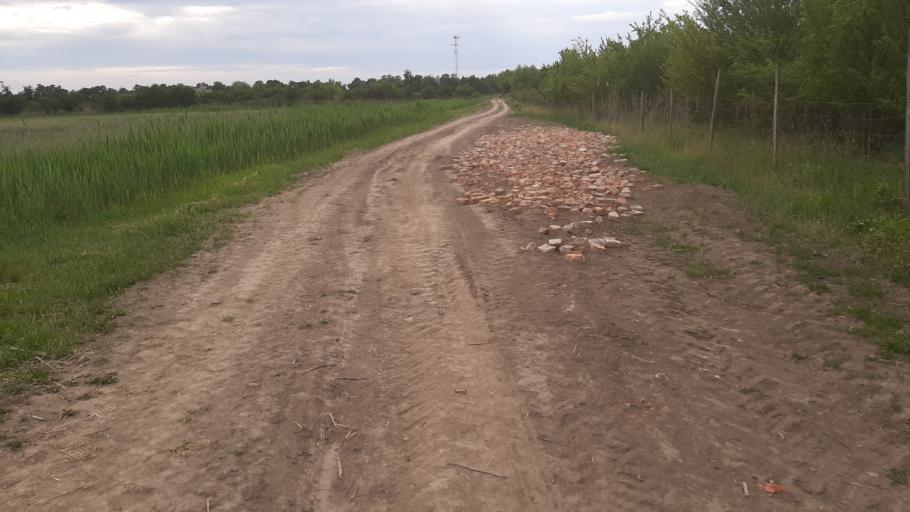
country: HU
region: Csongrad
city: Deszk
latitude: 46.1674
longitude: 20.1842
